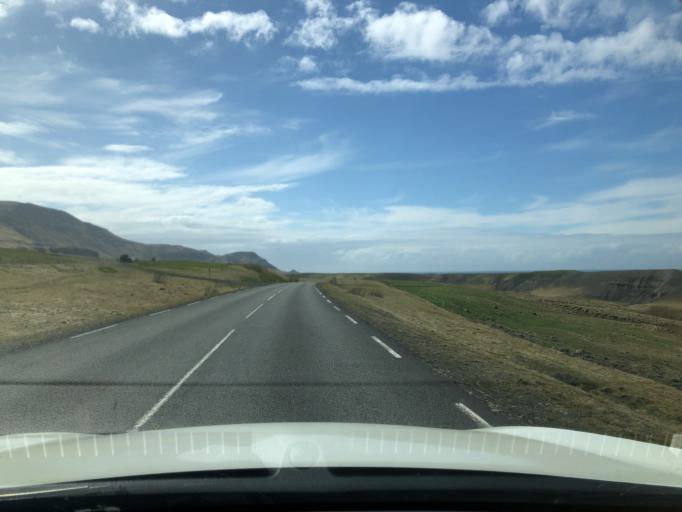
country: IS
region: Capital Region
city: Mosfellsbaer
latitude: 64.3099
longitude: -21.7736
